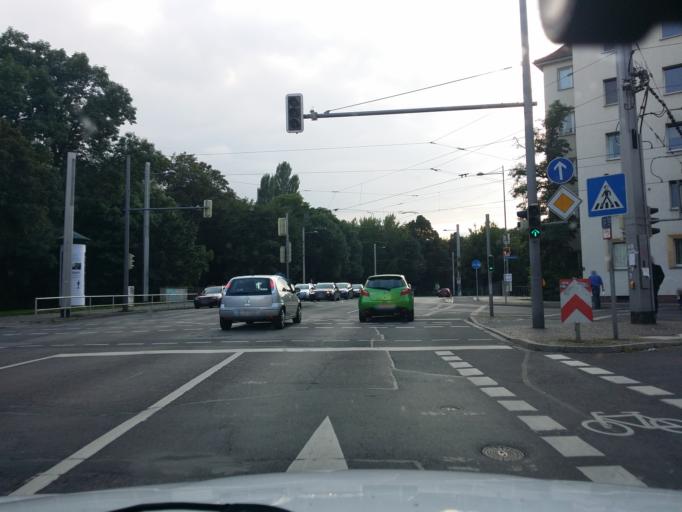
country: DE
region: Saxony
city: Leipzig
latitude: 51.3185
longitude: 12.3418
